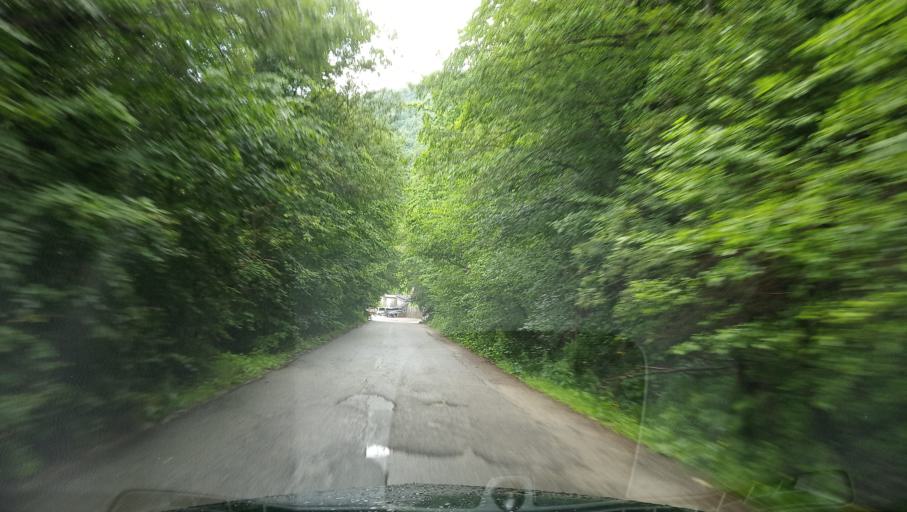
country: RO
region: Hunedoara
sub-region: Oras Petrila
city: Petrila
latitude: 45.3924
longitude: 23.4419
